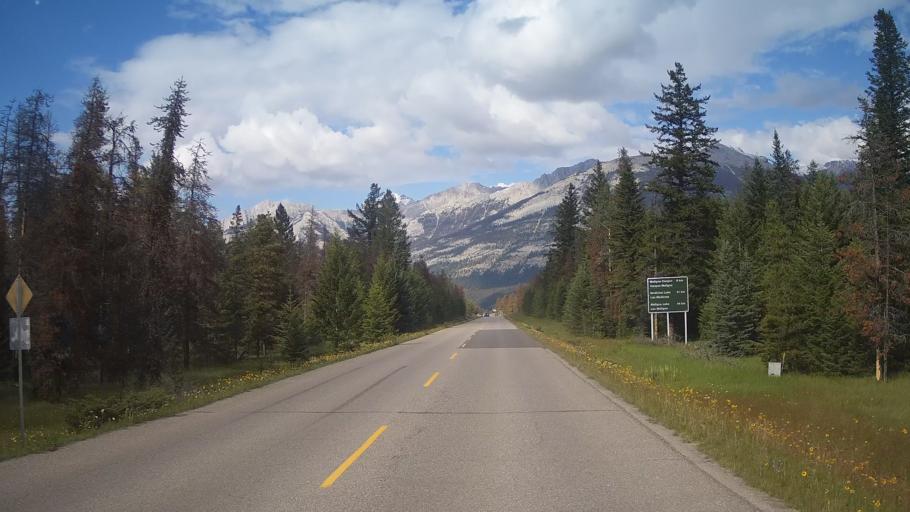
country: CA
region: Alberta
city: Jasper Park Lodge
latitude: 52.9109
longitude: -118.0535
